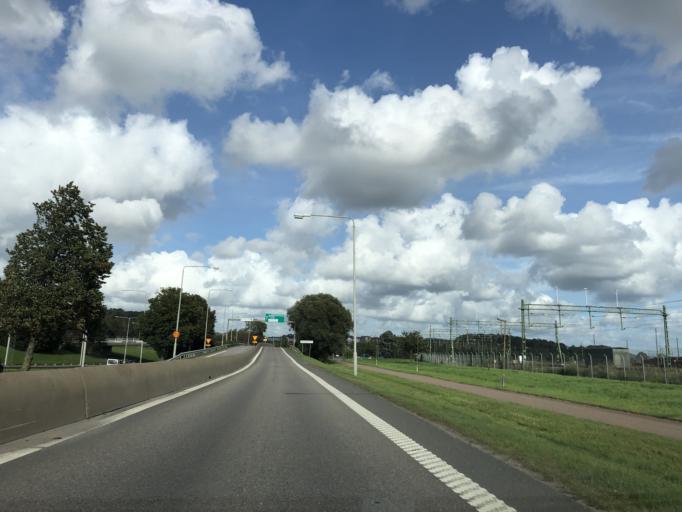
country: SE
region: Vaestra Goetaland
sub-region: Goteborg
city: Goeteborg
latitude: 57.7224
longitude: 11.9588
